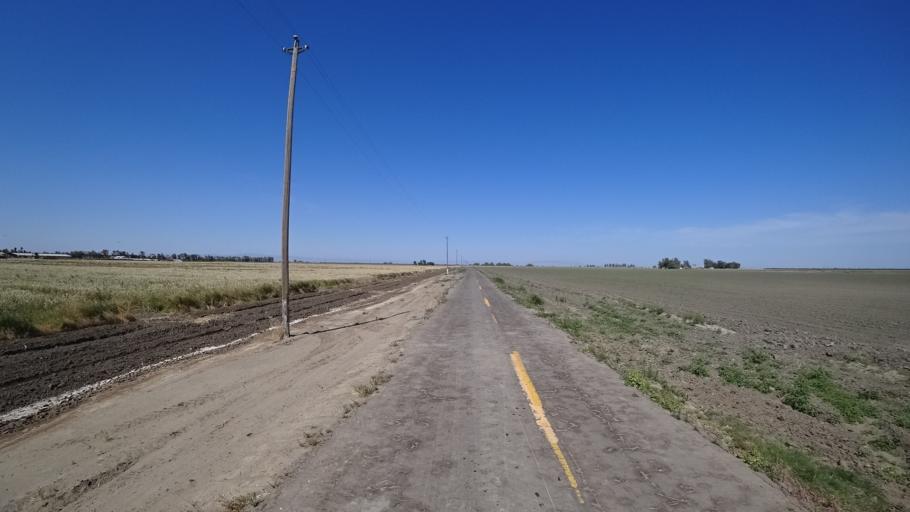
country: US
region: California
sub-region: Kings County
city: Stratford
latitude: 36.1968
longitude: -119.8267
